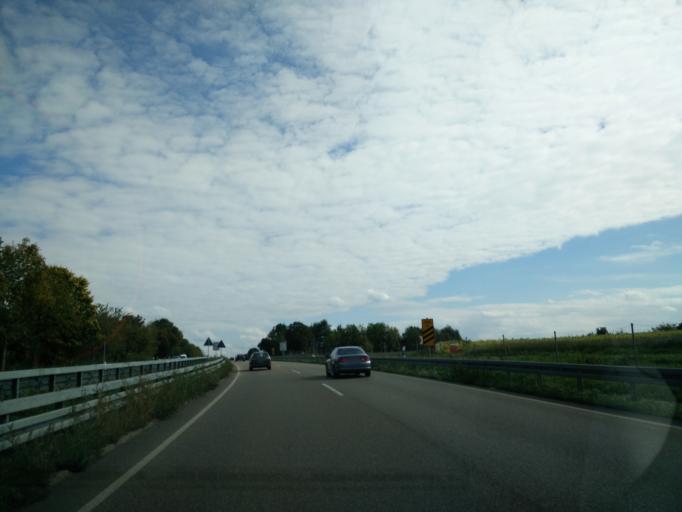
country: DE
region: Baden-Wuerttemberg
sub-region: Tuebingen Region
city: Kusterdingen
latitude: 48.5078
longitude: 9.1002
